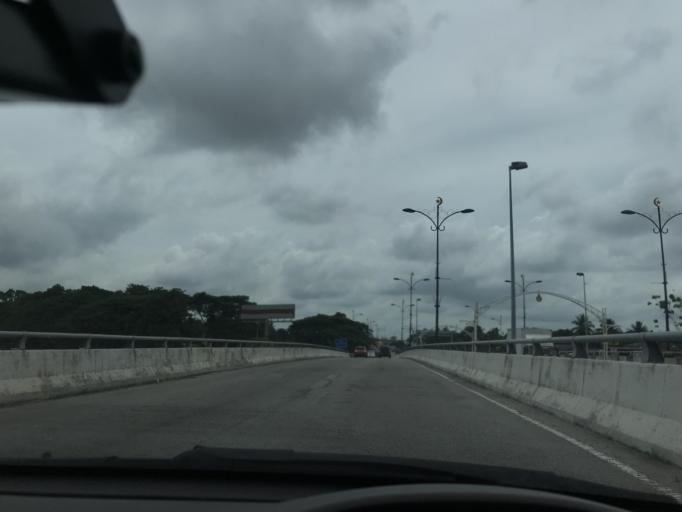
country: MY
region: Kelantan
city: Kota Bharu
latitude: 6.1164
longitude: 102.2274
